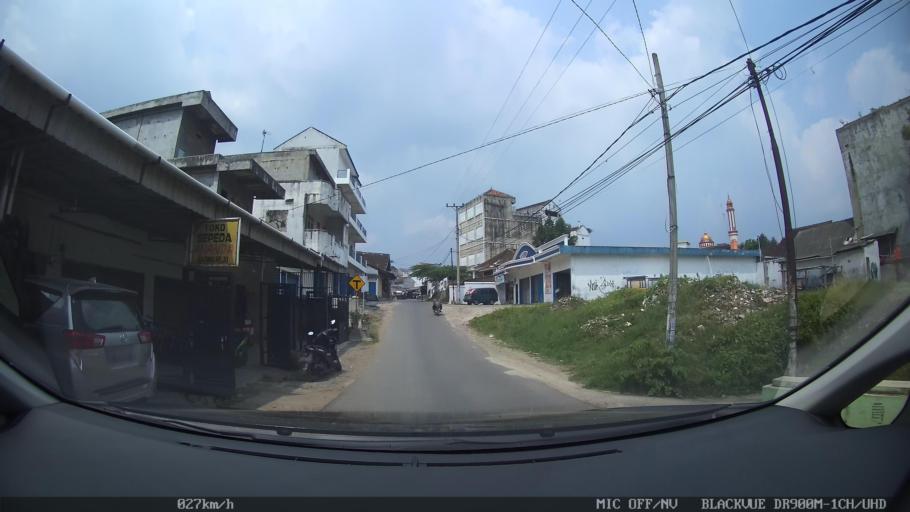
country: ID
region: Lampung
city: Gadingrejo
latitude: -5.3740
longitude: 105.0591
